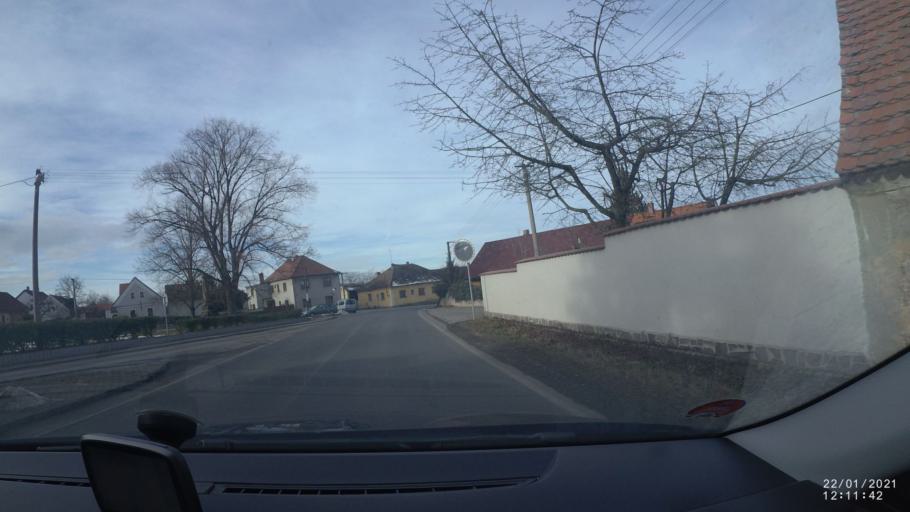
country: CZ
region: Plzensky
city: Dysina
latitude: 49.7522
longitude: 13.4877
